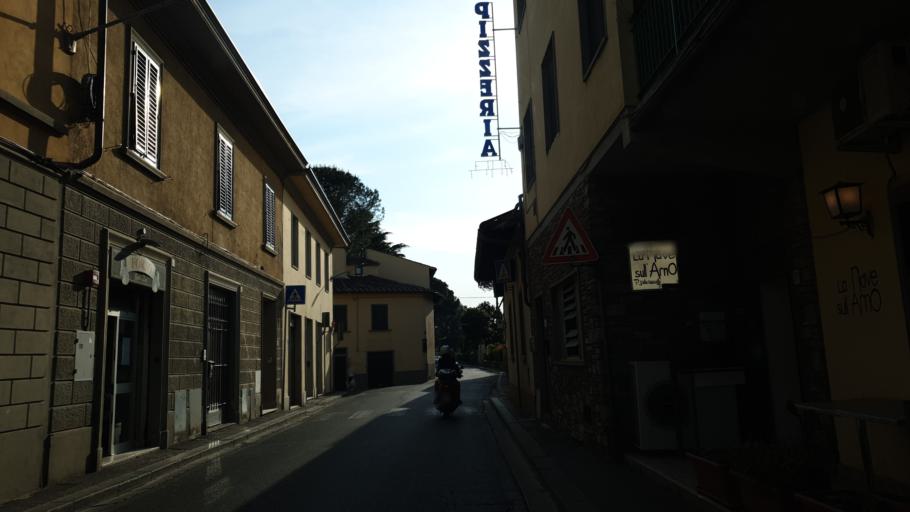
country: IT
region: Tuscany
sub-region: Province of Florence
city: Bagno a Ripoli
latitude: 43.7616
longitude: 11.3095
